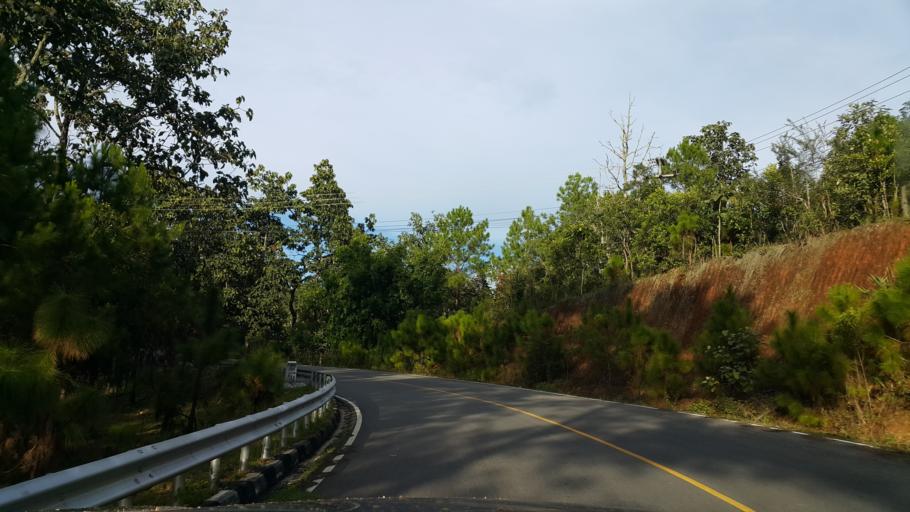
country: TH
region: Chiang Mai
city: Chaem Luang
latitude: 19.0982
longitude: 98.3469
